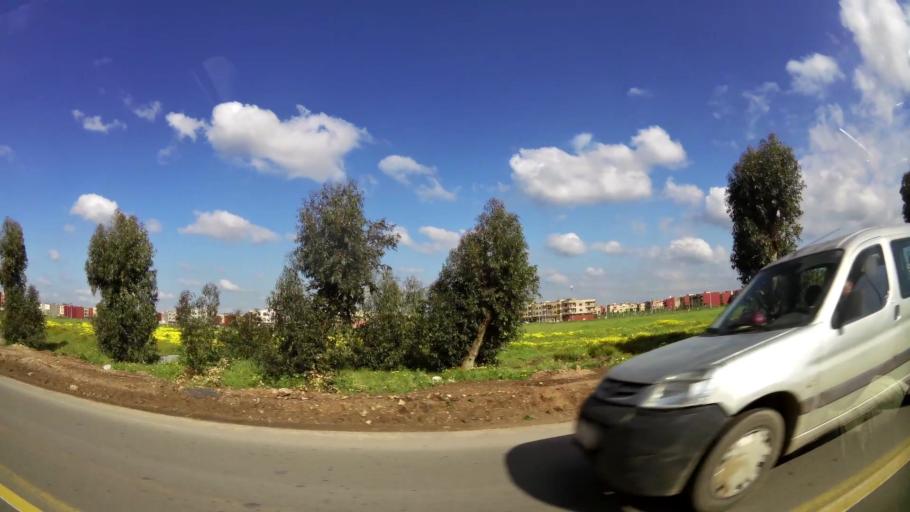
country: MA
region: Grand Casablanca
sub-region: Mediouna
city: Mediouna
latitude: 33.3790
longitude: -7.5406
